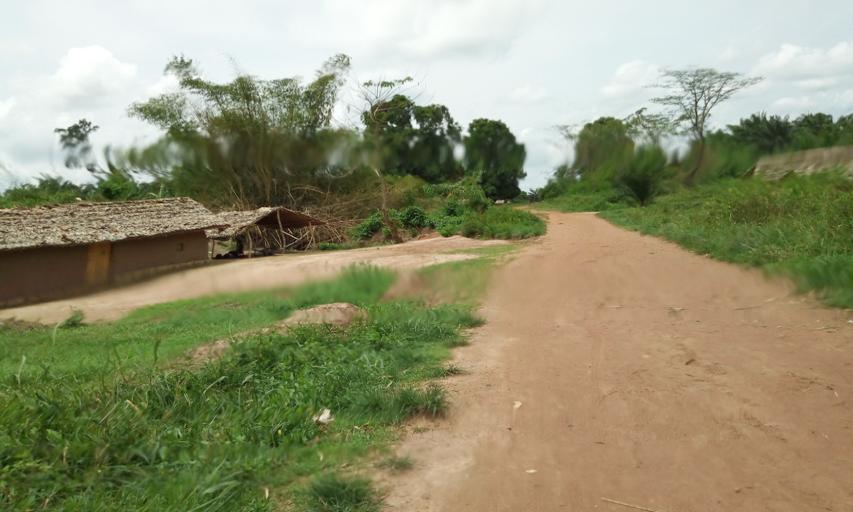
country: CD
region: Eastern Province
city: Bondo
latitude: 3.3705
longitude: 23.9086
